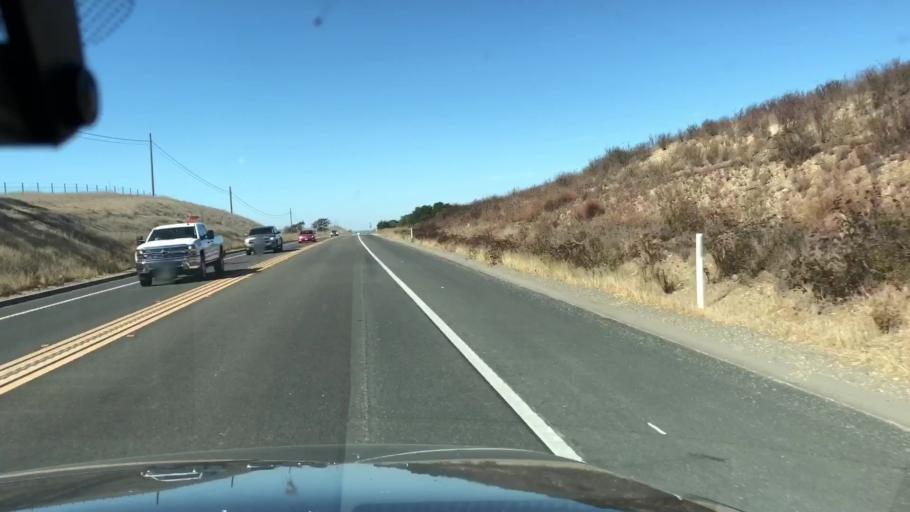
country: US
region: California
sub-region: Santa Barbara County
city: Santa Ynez
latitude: 34.5987
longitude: -120.0422
